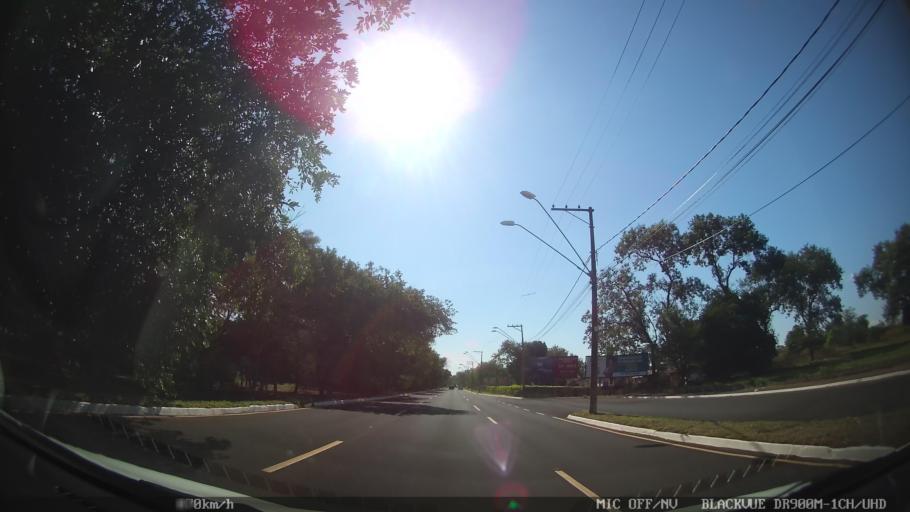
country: BR
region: Sao Paulo
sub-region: Ribeirao Preto
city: Ribeirao Preto
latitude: -21.2325
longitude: -47.7654
